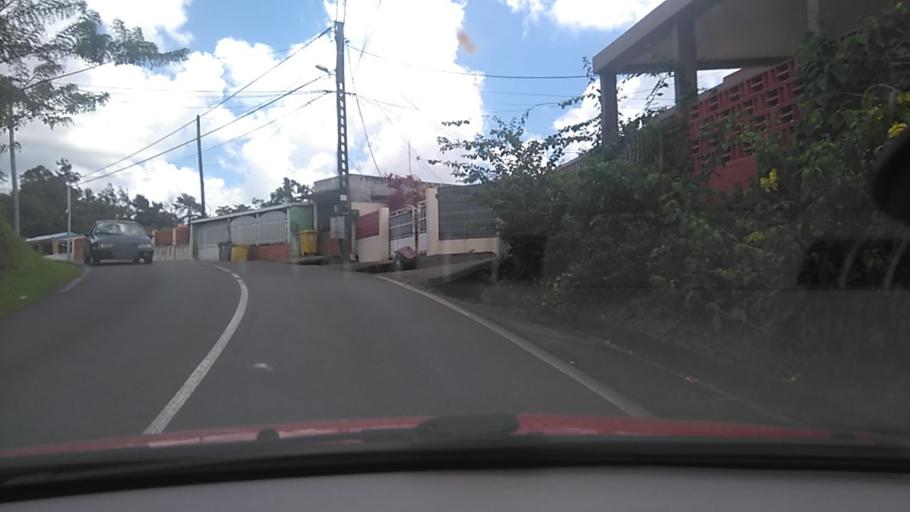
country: MQ
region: Martinique
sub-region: Martinique
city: Saint-Esprit
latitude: 14.5668
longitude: -60.9431
